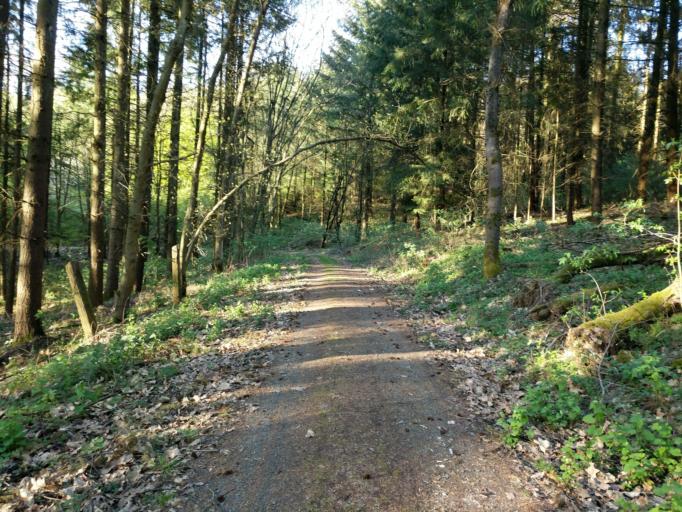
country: DE
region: Hesse
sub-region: Regierungsbezirk Giessen
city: Bad Endbach
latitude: 50.7604
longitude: 8.4853
